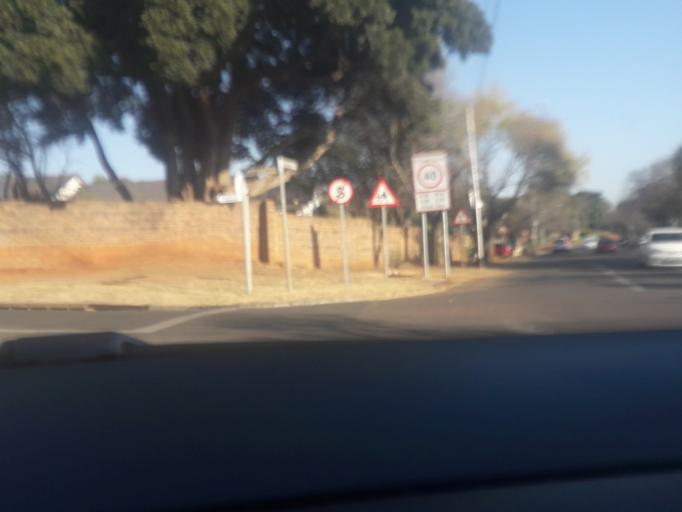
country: ZA
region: Gauteng
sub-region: City of Tshwane Metropolitan Municipality
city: Pretoria
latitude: -25.7646
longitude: 28.2600
